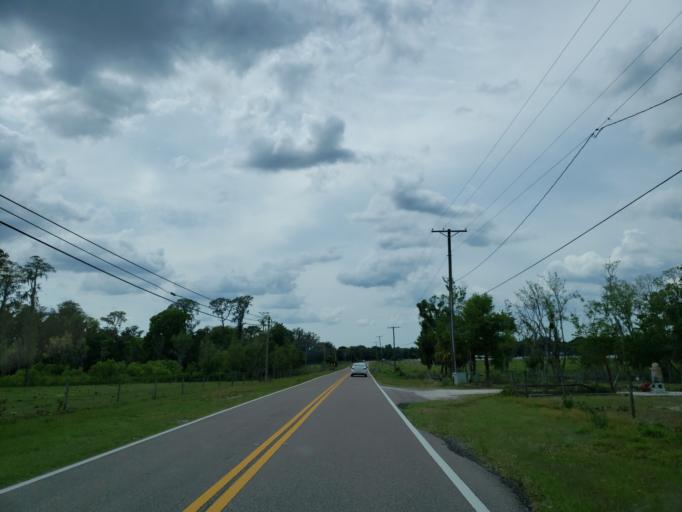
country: US
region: Florida
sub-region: Hillsborough County
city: Citrus Park
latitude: 28.1080
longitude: -82.5987
